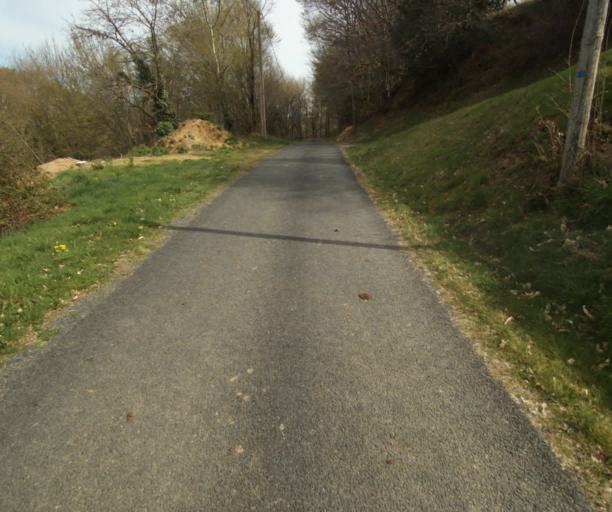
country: FR
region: Limousin
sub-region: Departement de la Correze
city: Naves
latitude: 45.3286
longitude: 1.8004
